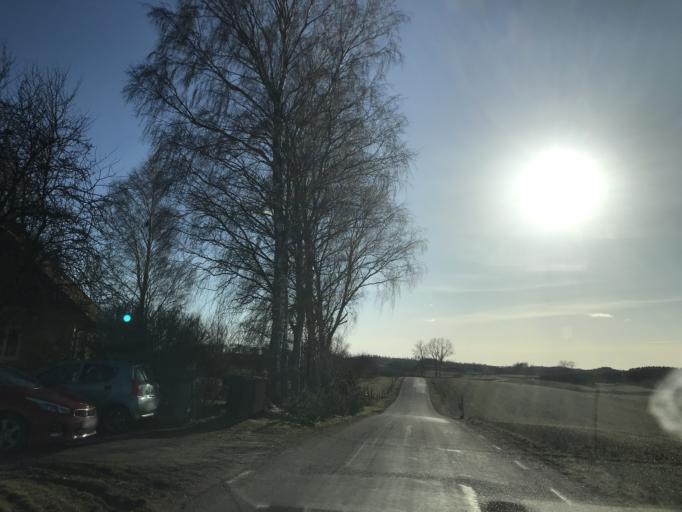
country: SE
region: Skane
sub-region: Ystads Kommun
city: Ystad
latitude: 55.5362
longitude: 13.7860
